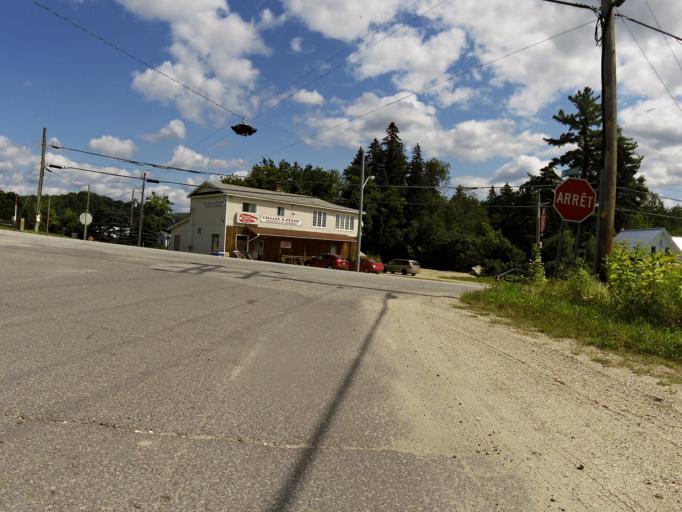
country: CA
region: Quebec
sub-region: Outaouais
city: Wakefield
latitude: 45.8132
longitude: -75.9534
